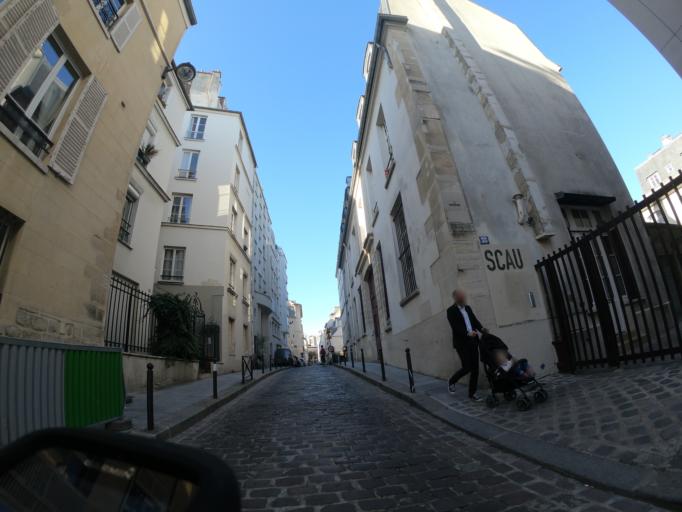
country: FR
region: Ile-de-France
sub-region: Paris
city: Paris
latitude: 48.8421
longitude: 2.3483
